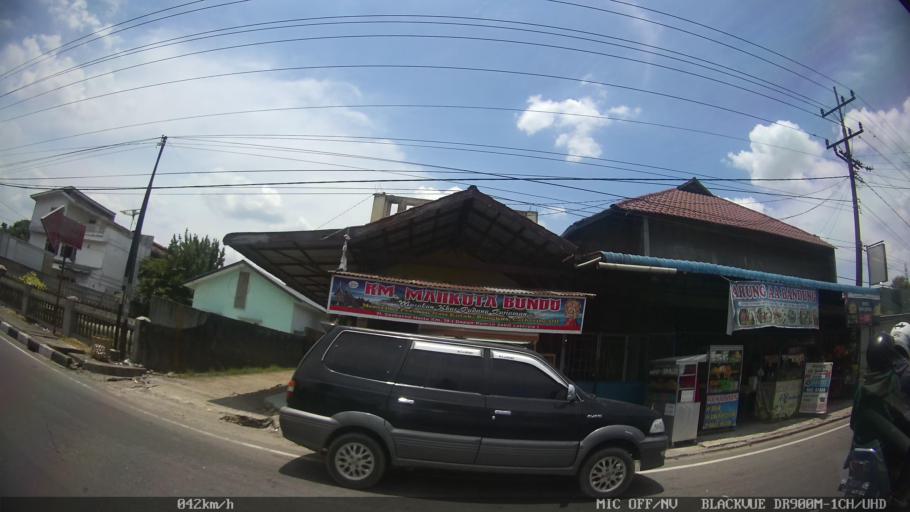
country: ID
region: North Sumatra
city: Binjai
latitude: 3.6065
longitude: 98.5268
